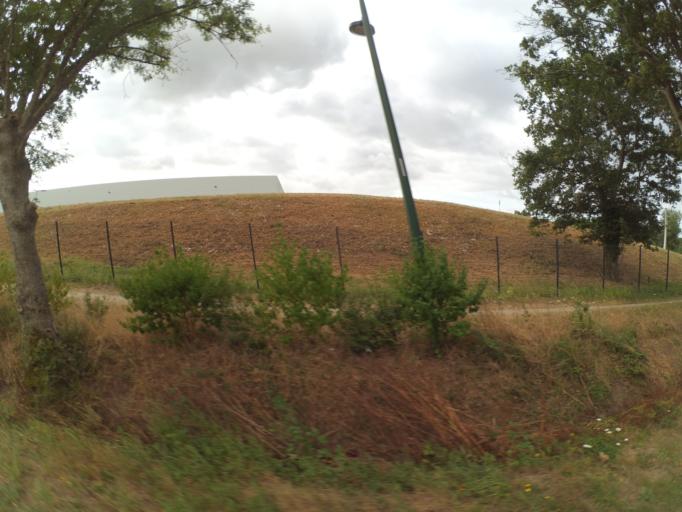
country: FR
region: Pays de la Loire
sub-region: Departement de la Vendee
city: La Bernardiere
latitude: 47.0571
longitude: -1.2604
